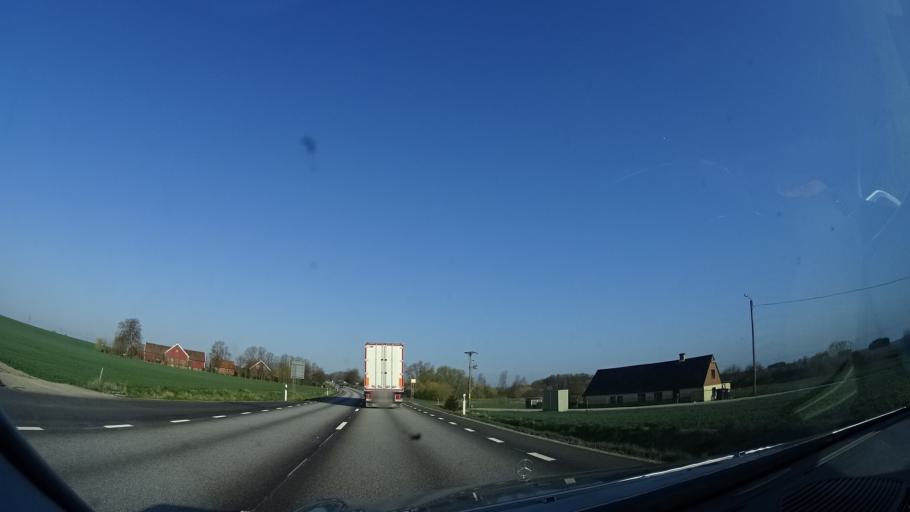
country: SE
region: Skane
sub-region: Eslovs Kommun
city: Eslov
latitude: 55.8557
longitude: 13.2708
